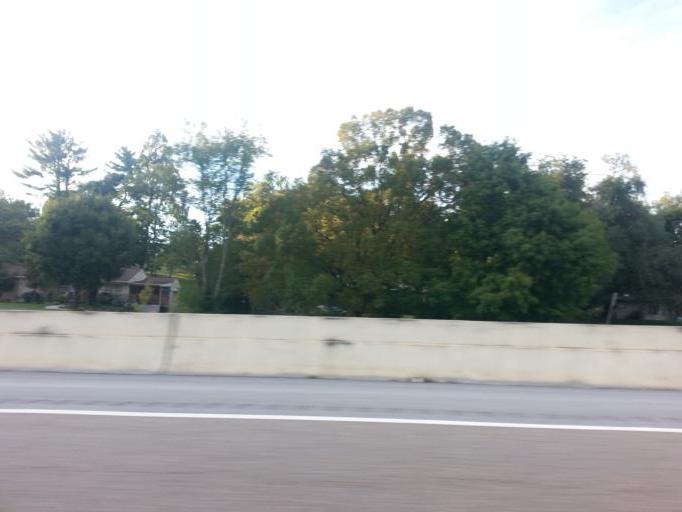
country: US
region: Tennessee
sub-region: Knox County
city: Knoxville
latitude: 35.9470
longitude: -83.9947
